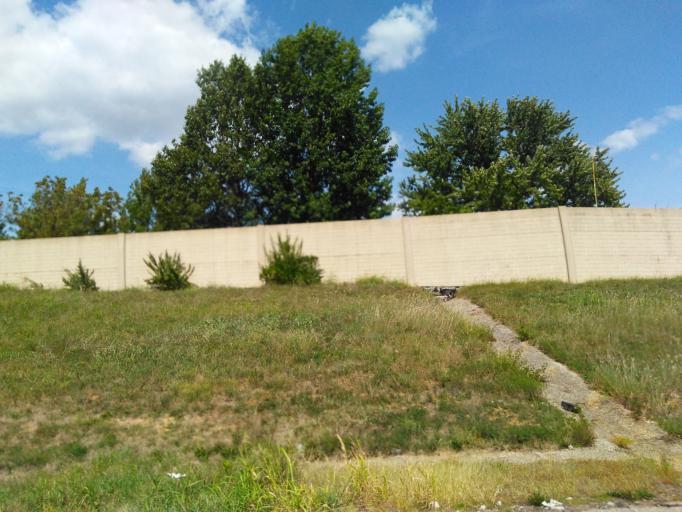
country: US
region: Missouri
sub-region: Saint Louis County
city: Concord
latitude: 38.5096
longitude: -90.3577
